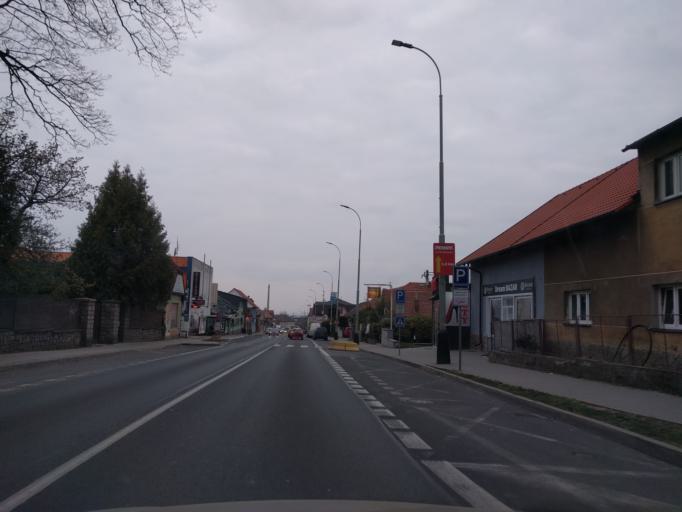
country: CZ
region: Central Bohemia
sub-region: Okres Praha-Vychod
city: Ricany
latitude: 49.9988
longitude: 14.6691
